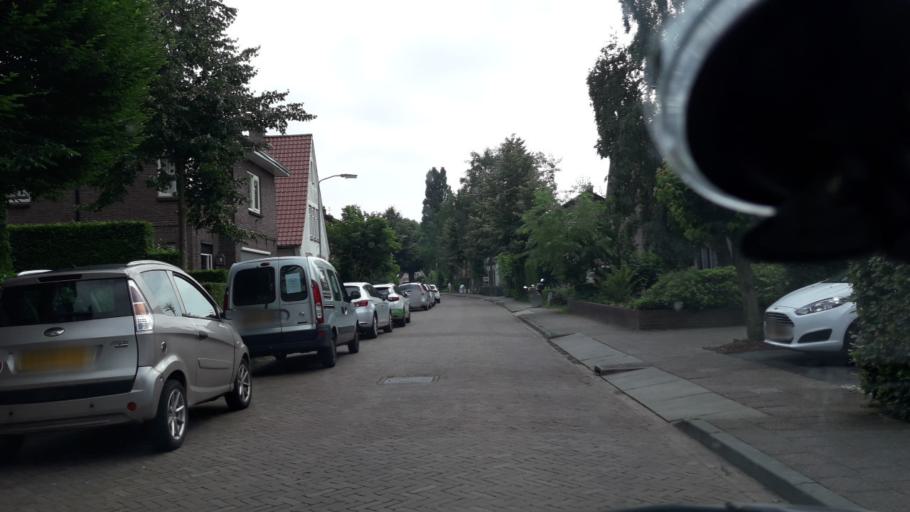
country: NL
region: Gelderland
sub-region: Gemeente Ermelo
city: Ermelo
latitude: 52.3001
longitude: 5.6153
